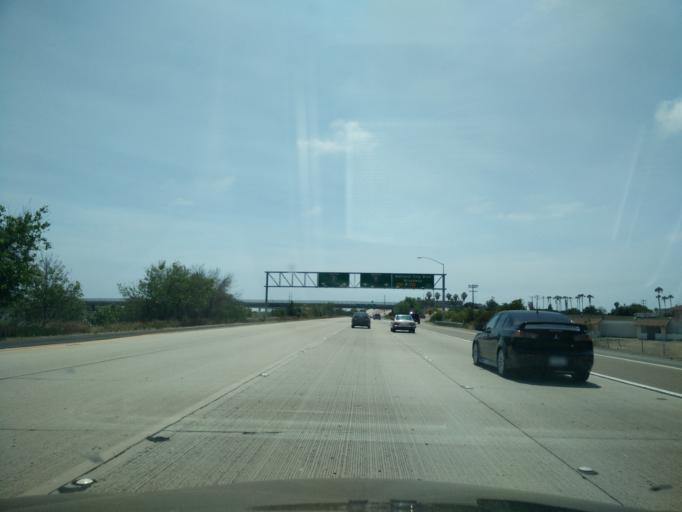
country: US
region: California
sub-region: San Diego County
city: Chula Vista
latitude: 32.6544
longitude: -117.0944
